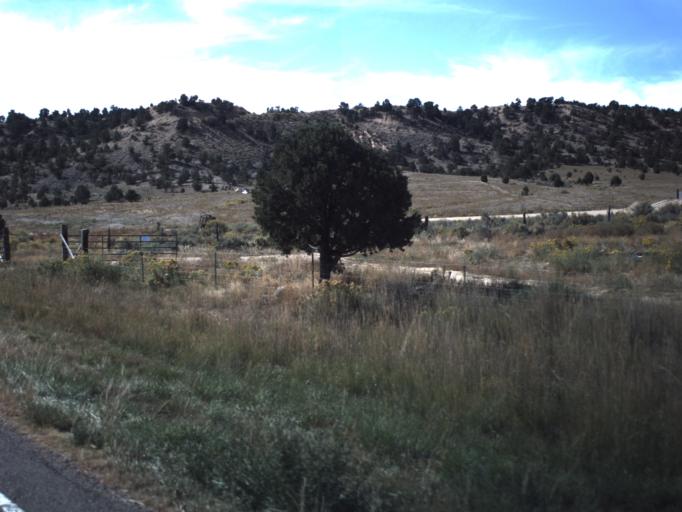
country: US
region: Utah
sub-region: Garfield County
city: Panguitch
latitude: 37.6179
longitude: -112.0770
